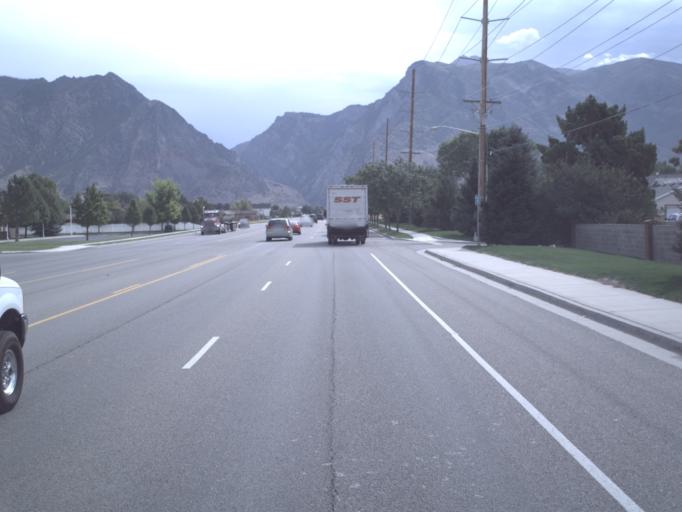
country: US
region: Utah
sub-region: Utah County
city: Alpine
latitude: 40.4318
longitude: -111.7998
